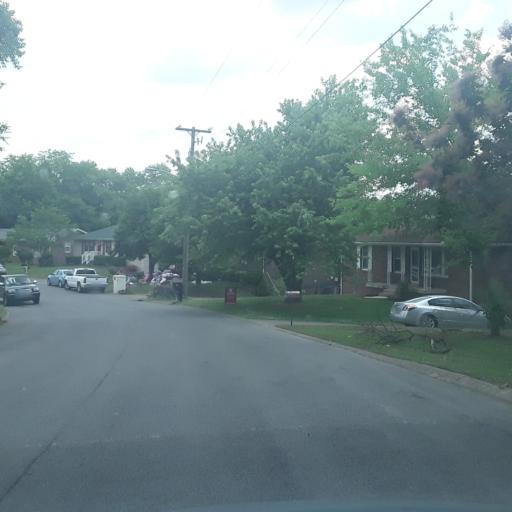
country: US
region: Tennessee
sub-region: Williamson County
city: Brentwood Estates
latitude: 36.0562
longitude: -86.6960
